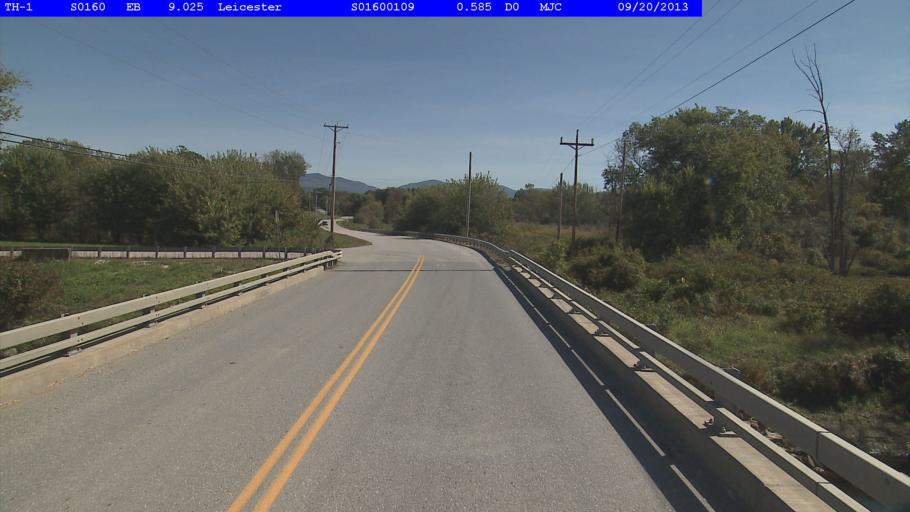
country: US
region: Vermont
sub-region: Rutland County
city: Brandon
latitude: 43.8554
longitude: -73.1483
